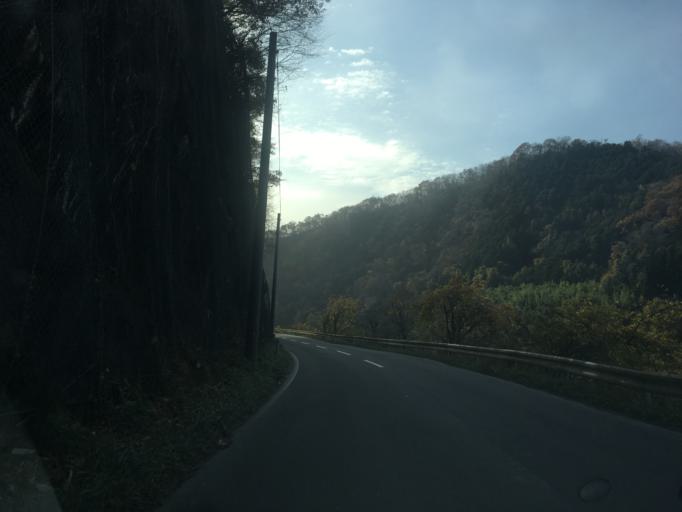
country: JP
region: Iwate
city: Ichinoseki
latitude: 38.9448
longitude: 141.2101
